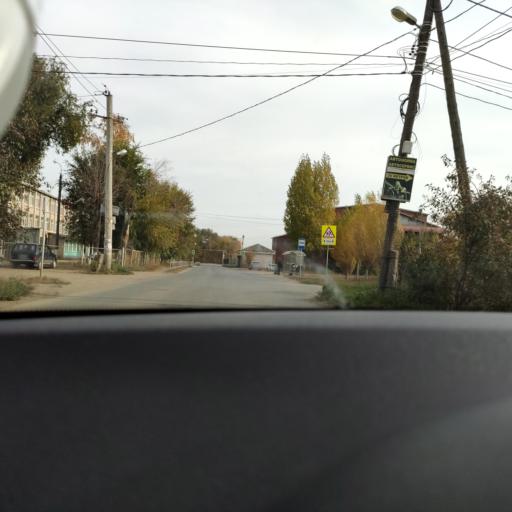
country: RU
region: Samara
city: Samara
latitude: 53.1836
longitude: 50.2408
